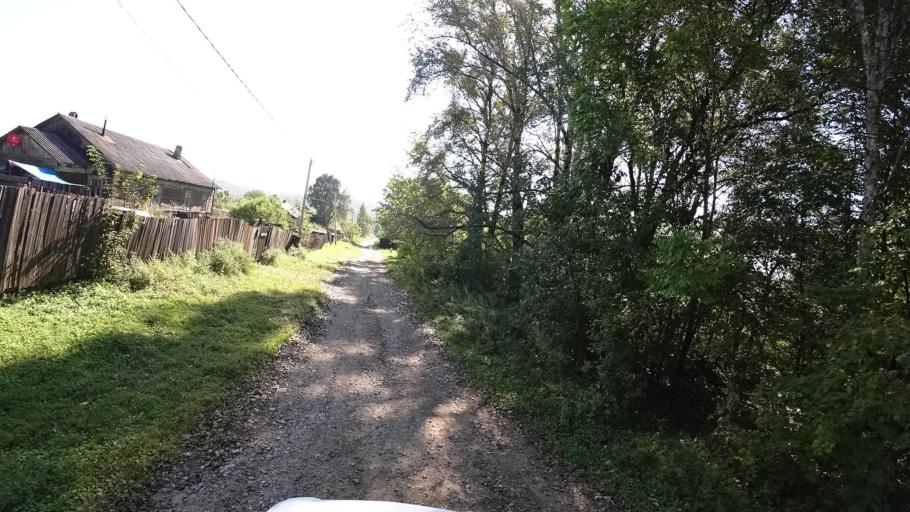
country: RU
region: Jewish Autonomous Oblast
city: Bira
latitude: 49.0012
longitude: 132.4699
